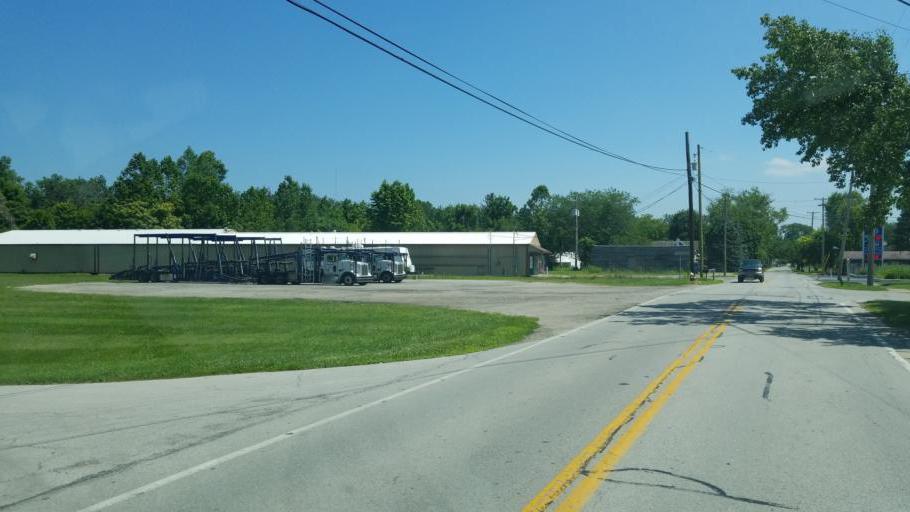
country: US
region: Ohio
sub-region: Erie County
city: Sandusky
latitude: 41.4055
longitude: -82.8112
